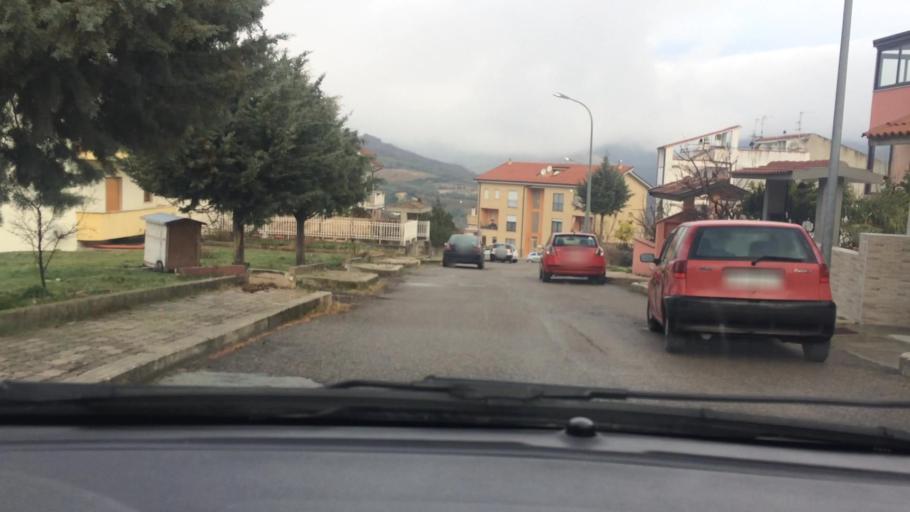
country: IT
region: Basilicate
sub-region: Provincia di Matera
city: San Mauro Forte
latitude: 40.4891
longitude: 16.2432
